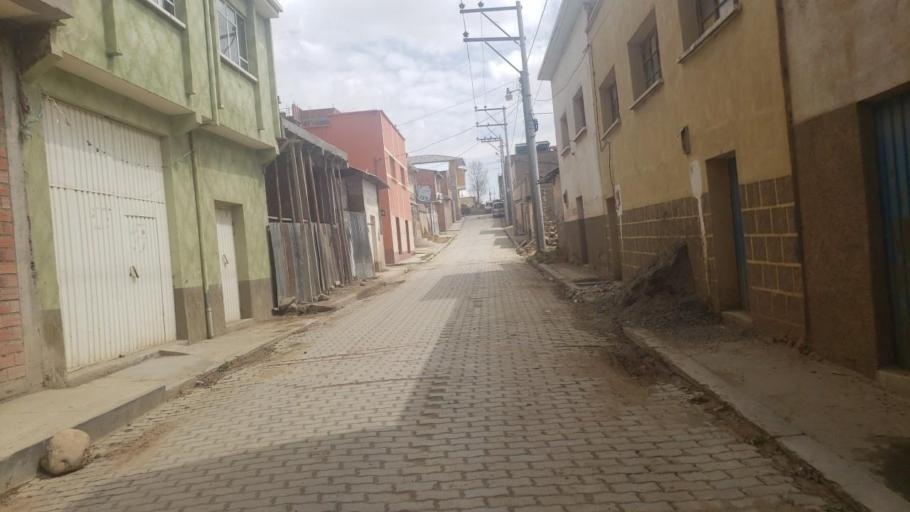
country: BO
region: La Paz
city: Batallas
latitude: -16.4008
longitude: -68.4770
